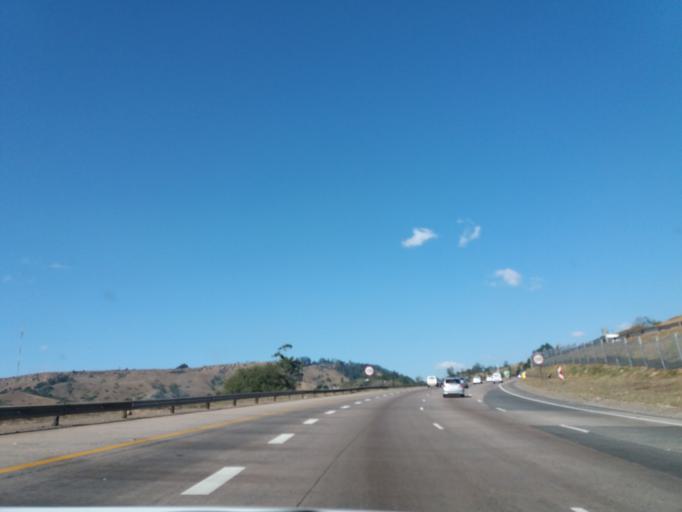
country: ZA
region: KwaZulu-Natal
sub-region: eThekwini Metropolitan Municipality
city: Mpumalanga
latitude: -29.7713
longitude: 30.6919
